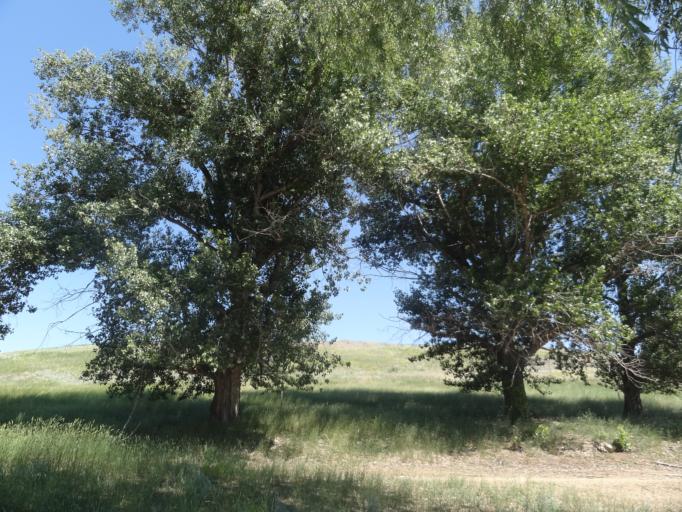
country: RU
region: Saratov
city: Krasnoarmeysk
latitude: 51.1487
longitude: 45.9329
